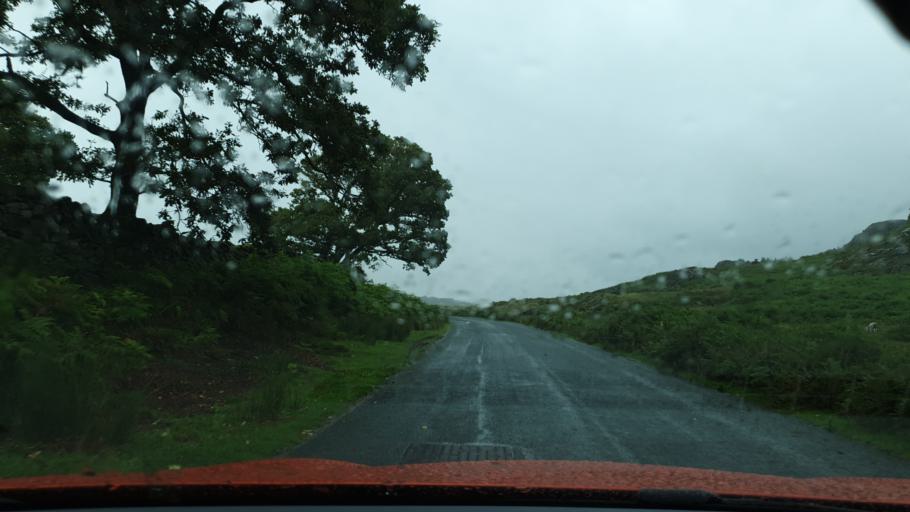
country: GB
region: England
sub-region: Cumbria
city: Millom
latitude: 54.3221
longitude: -3.2355
